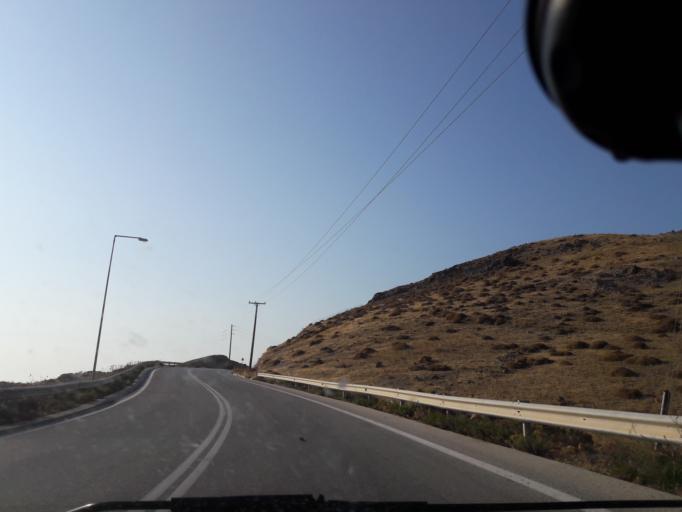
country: GR
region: North Aegean
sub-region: Nomos Lesvou
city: Myrina
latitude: 39.8652
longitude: 25.0562
